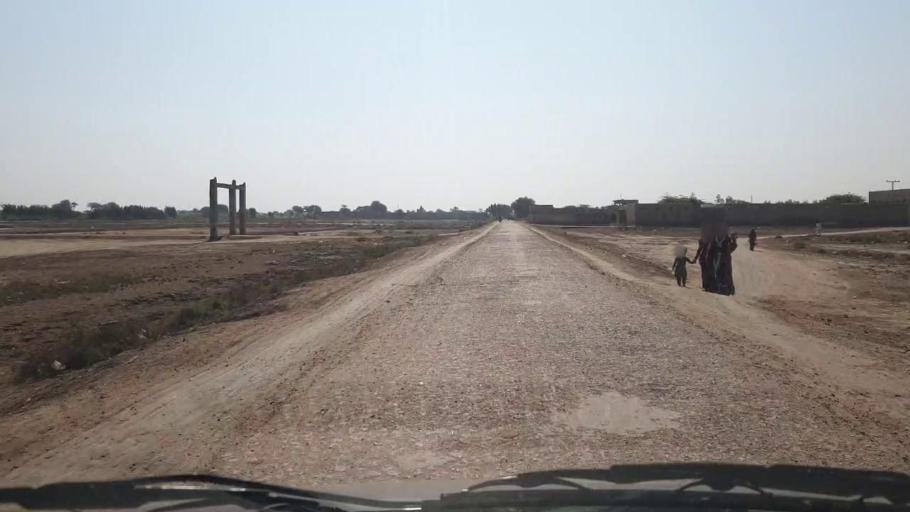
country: PK
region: Sindh
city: Samaro
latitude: 25.2785
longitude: 69.2510
